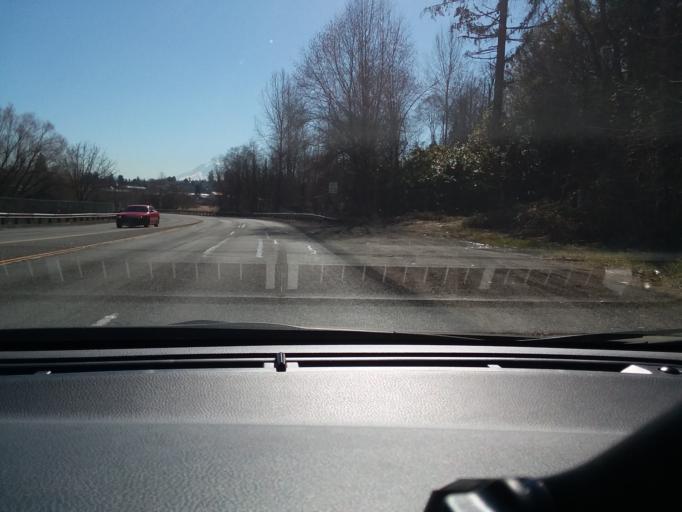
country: US
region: Washington
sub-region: Pierce County
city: Waller
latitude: 47.1910
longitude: -122.3358
